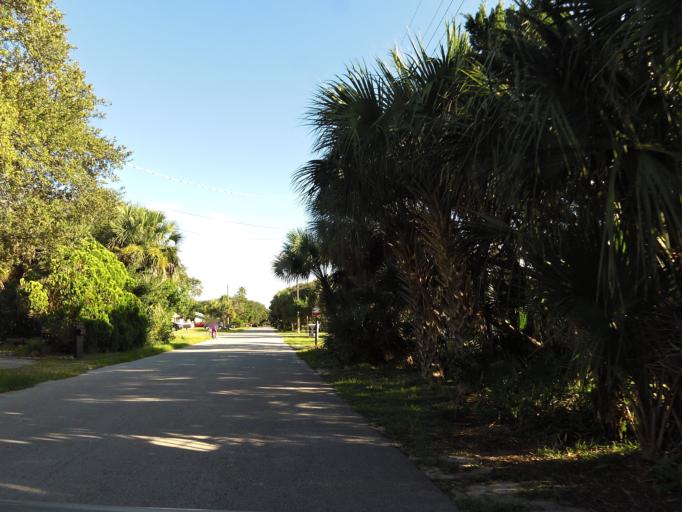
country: US
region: Florida
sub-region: Flagler County
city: Flagler Beach
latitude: 29.4612
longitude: -81.1216
